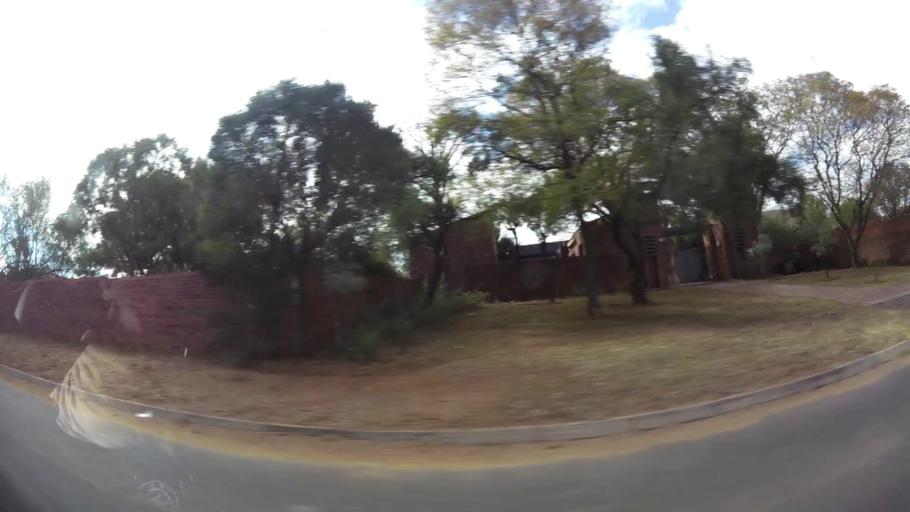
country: ZA
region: Gauteng
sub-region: West Rand District Municipality
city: Muldersdriseloop
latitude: -26.0855
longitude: 27.8540
